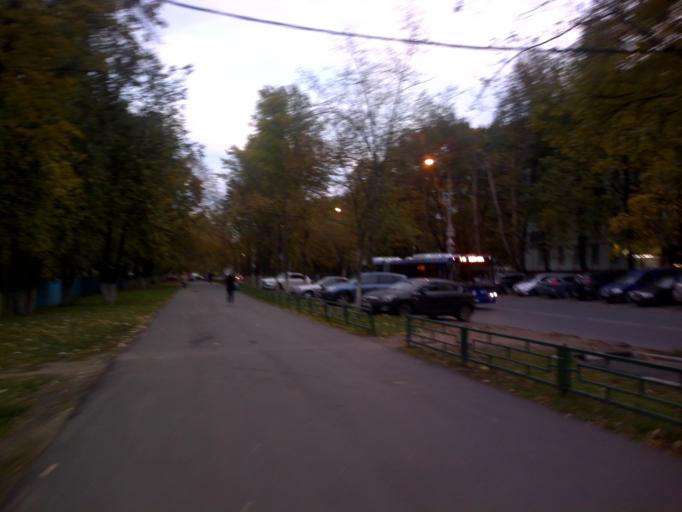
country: RU
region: Moscow
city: Novyye Cheremushki
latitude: 55.6931
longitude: 37.5843
